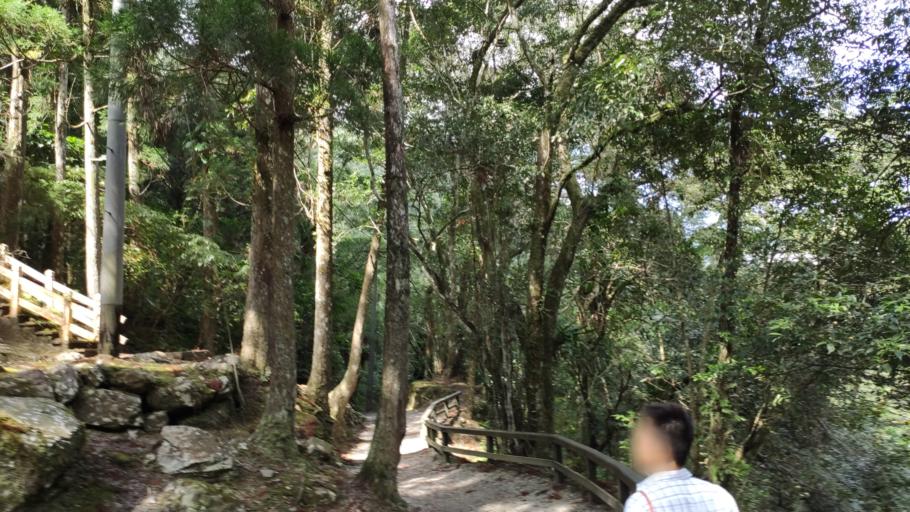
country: TW
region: Taiwan
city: Daxi
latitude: 24.8213
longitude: 121.4499
